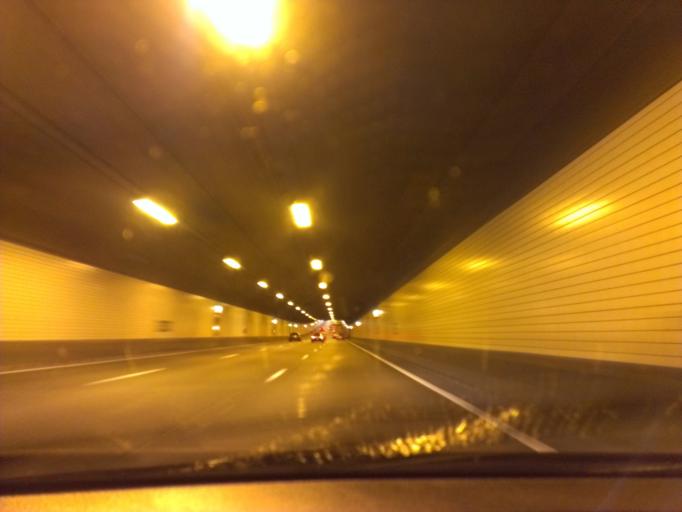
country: NL
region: South Holland
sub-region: Gemeente Alblasserdam
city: Alblasserdam
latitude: 51.8578
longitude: 4.6572
